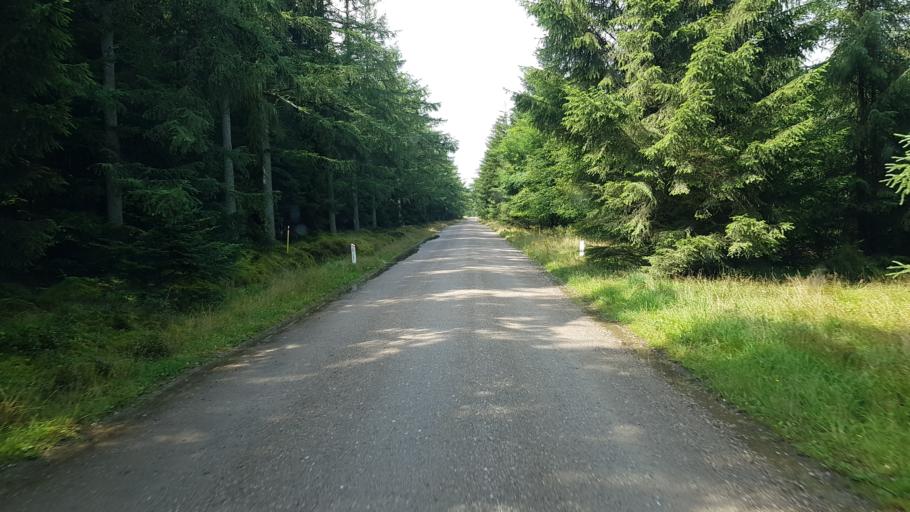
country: DK
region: South Denmark
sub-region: Vejen Kommune
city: Holsted
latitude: 55.5943
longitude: 8.9125
